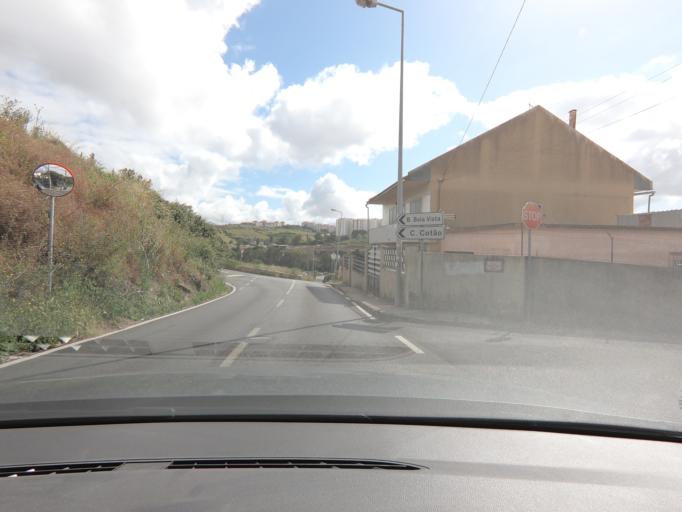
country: PT
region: Lisbon
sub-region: Sintra
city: Cacem
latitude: 38.7523
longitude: -9.2946
